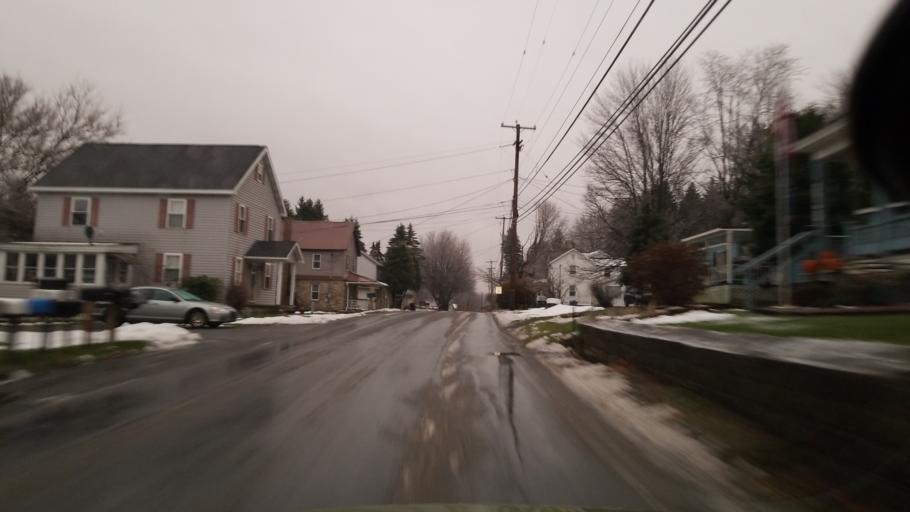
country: US
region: Pennsylvania
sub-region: Clearfield County
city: Clearfield
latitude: 41.0400
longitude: -78.4564
